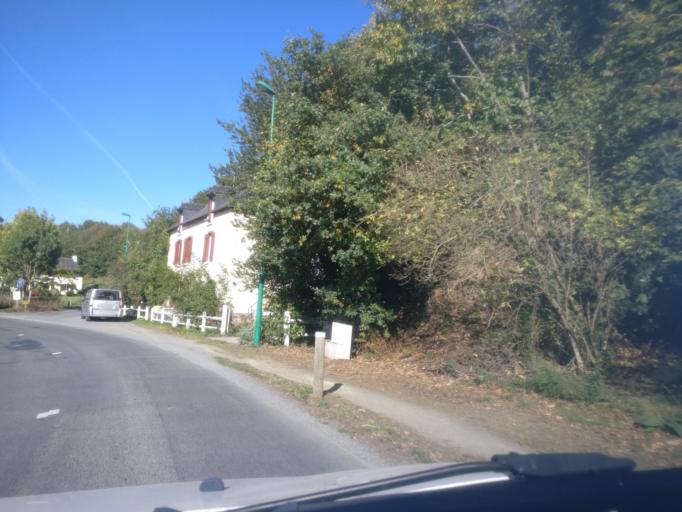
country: FR
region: Brittany
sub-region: Departement d'Ille-et-Vilaine
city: Chevaigne
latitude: 48.2091
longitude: -1.6337
